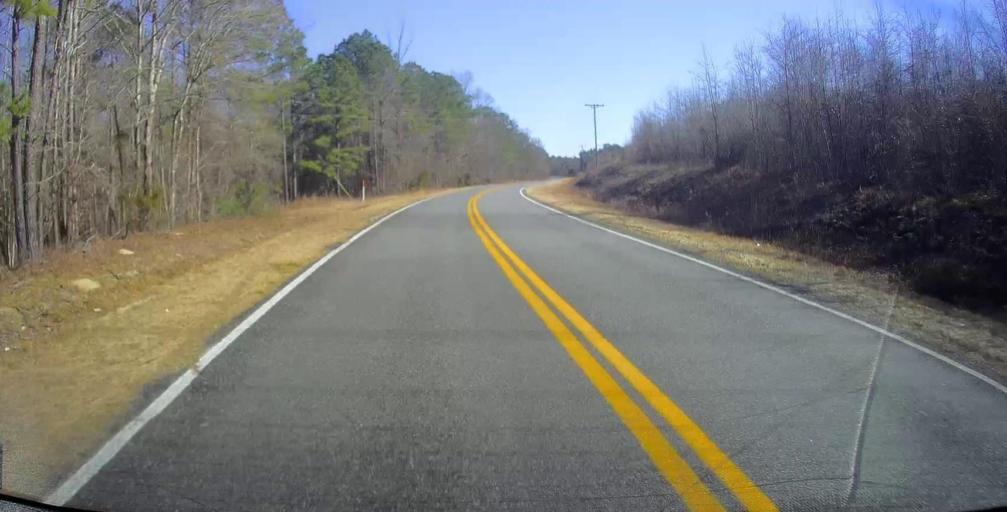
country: US
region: Georgia
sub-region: Crawford County
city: Knoxville
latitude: 32.7059
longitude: -83.9944
